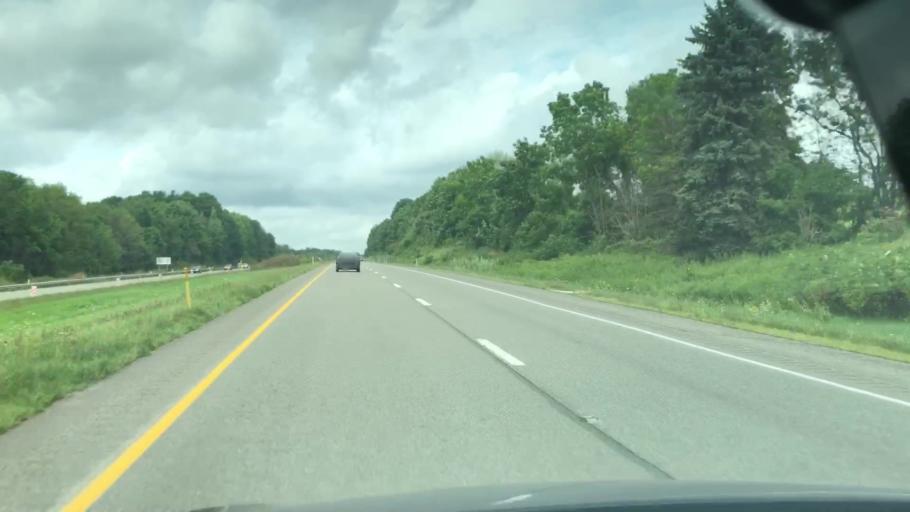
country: US
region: Pennsylvania
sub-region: Crawford County
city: Meadville
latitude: 41.5587
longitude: -80.1811
